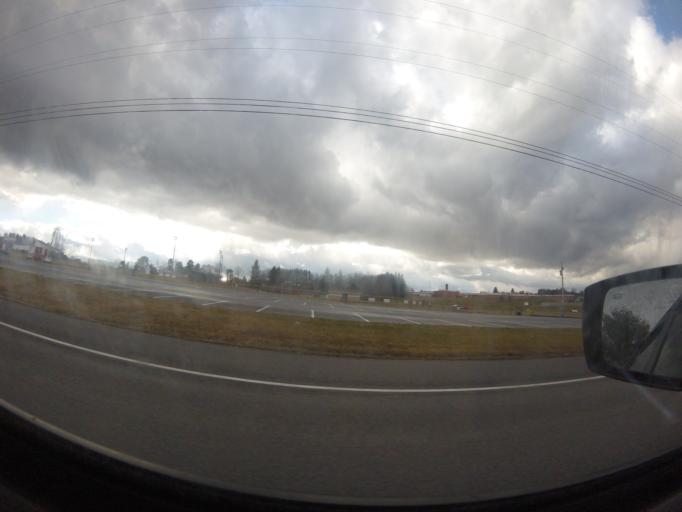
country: US
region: Maryland
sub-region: Garrett County
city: Mountain Lake Park
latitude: 39.4067
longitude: -79.3865
